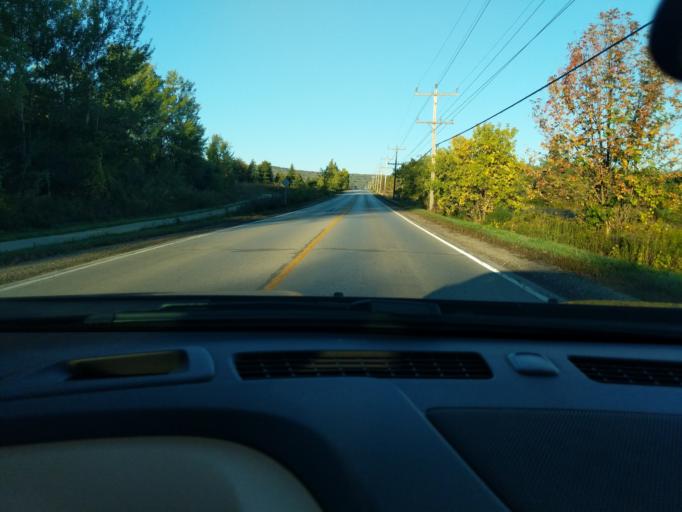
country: CA
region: Ontario
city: Collingwood
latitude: 44.4987
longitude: -80.2568
